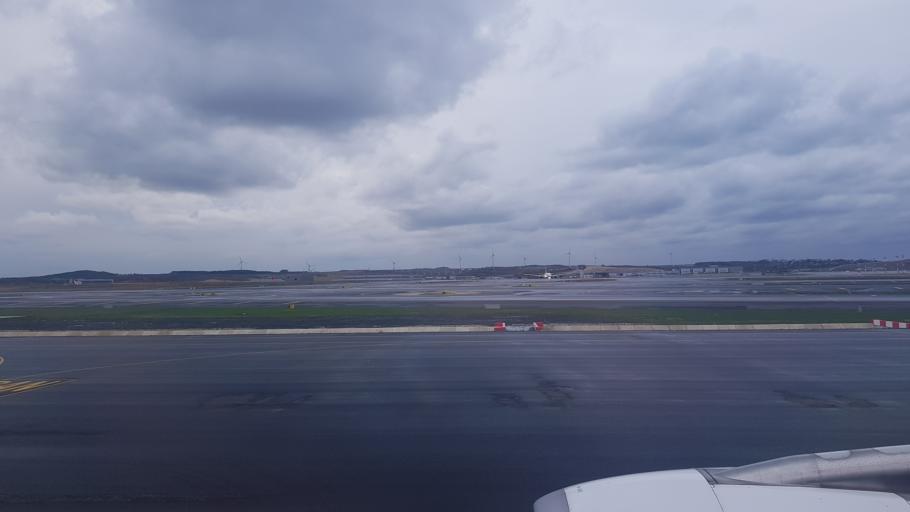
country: TR
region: Istanbul
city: Durusu
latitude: 41.2644
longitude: 28.7343
